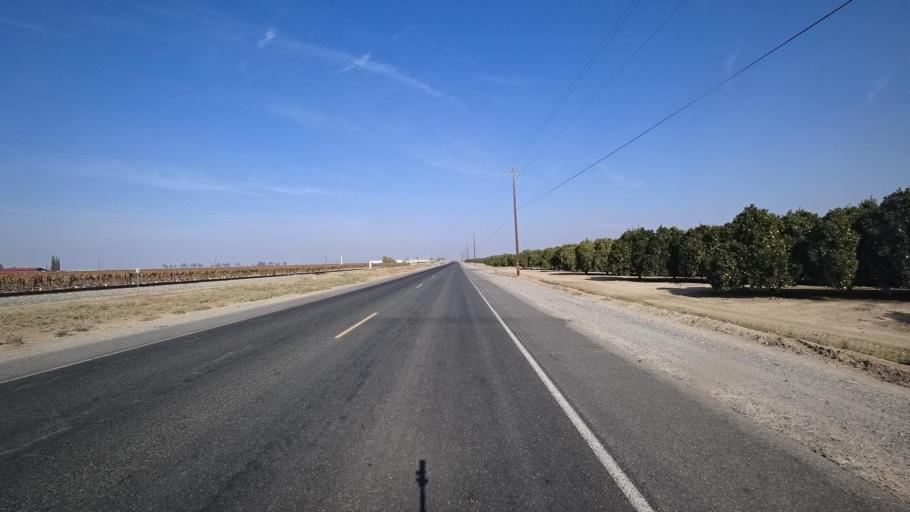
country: US
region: California
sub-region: Kern County
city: McFarland
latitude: 35.6709
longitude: -119.1886
